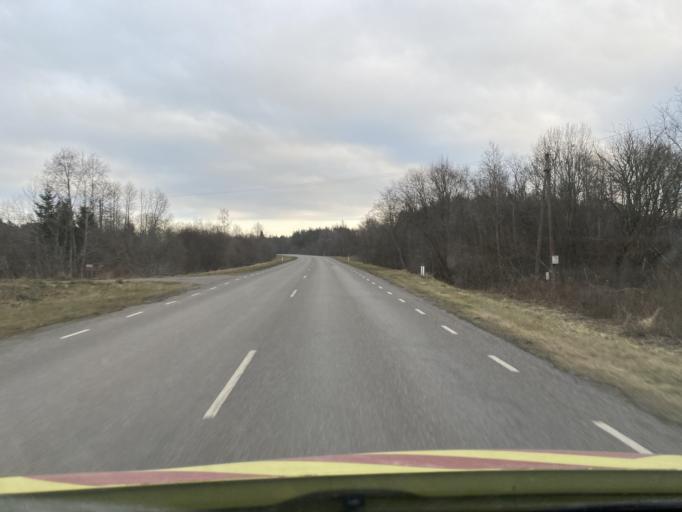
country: EE
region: Laeaene
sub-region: Lihula vald
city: Lihula
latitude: 58.7871
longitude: 23.8829
